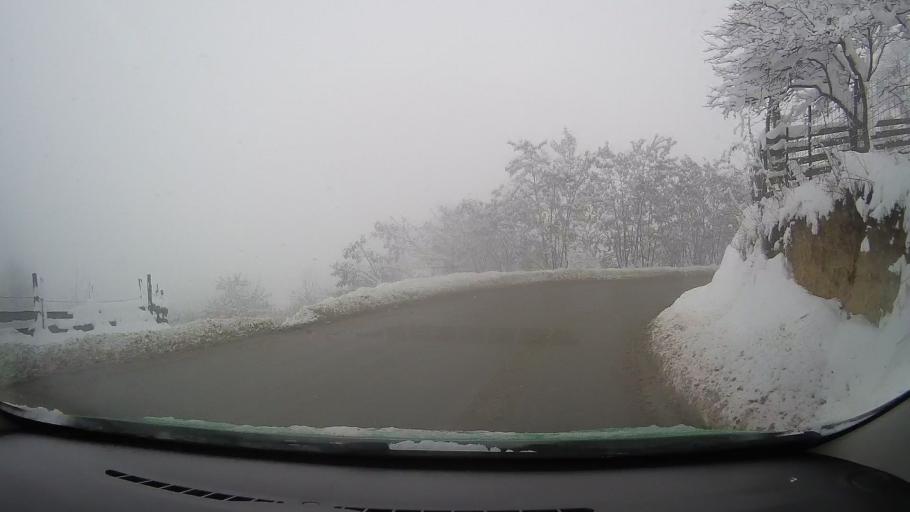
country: RO
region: Sibiu
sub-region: Comuna Jina
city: Jina
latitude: 45.7851
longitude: 23.6895
